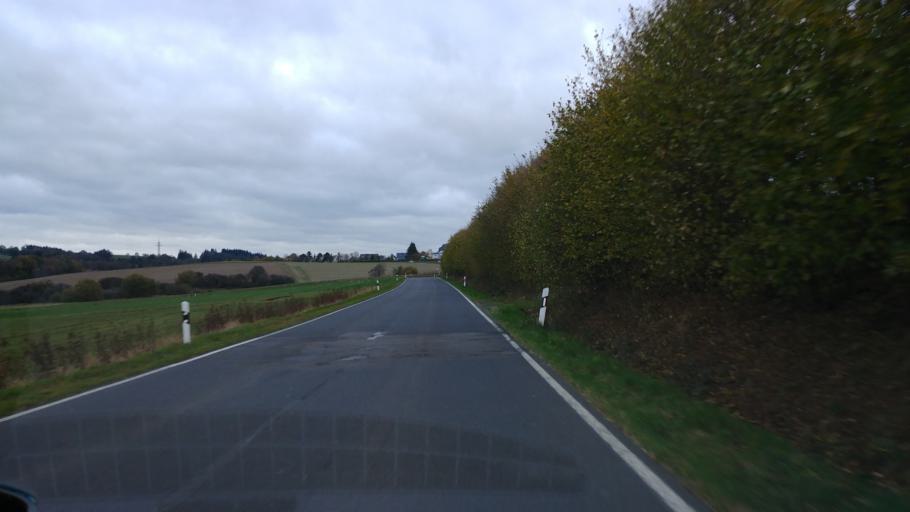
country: DE
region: Rheinland-Pfalz
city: Morbach
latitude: 49.8074
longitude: 7.1082
